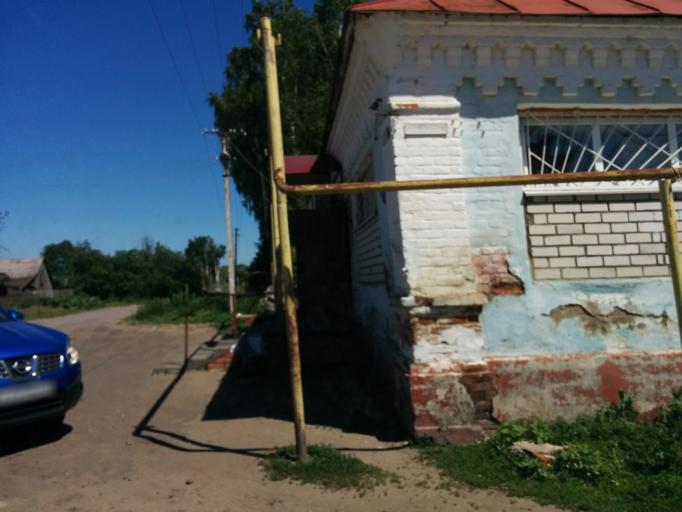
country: RU
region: Tambov
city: Morshansk
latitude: 53.6193
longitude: 41.8508
